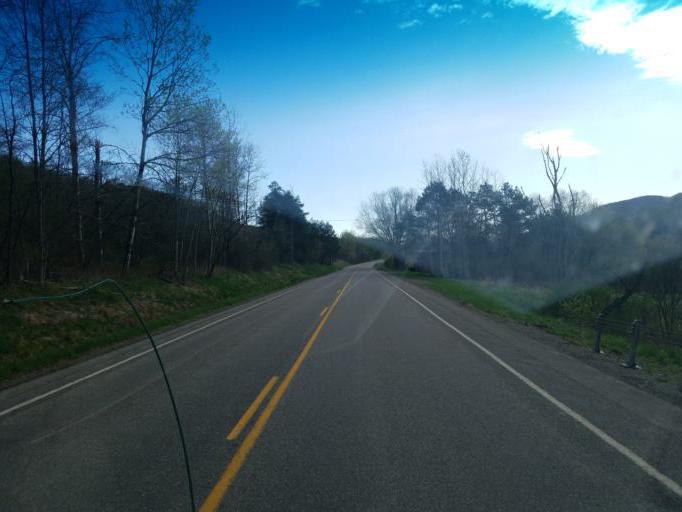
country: US
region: New York
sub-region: Allegany County
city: Andover
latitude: 42.0161
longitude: -77.8308
